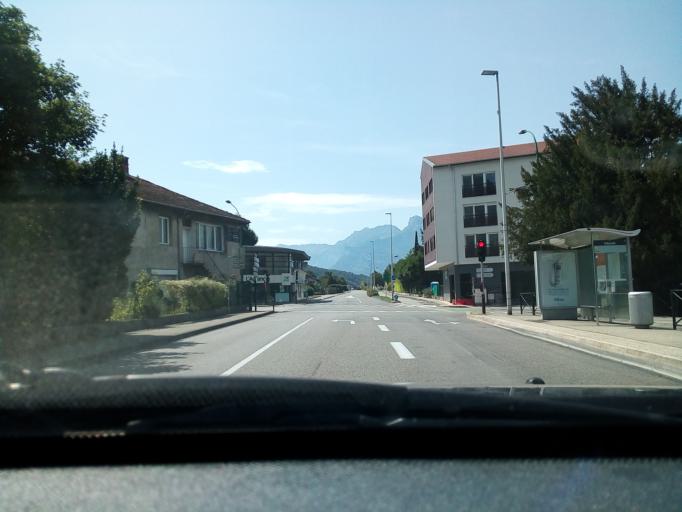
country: FR
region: Rhone-Alpes
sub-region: Departement de l'Isere
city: Eybens
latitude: 45.1530
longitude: 5.7492
